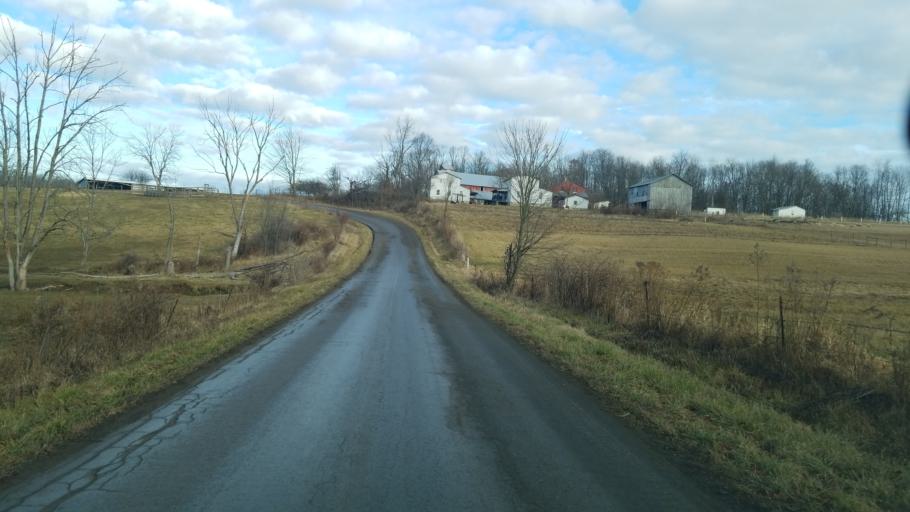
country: US
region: Ohio
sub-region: Knox County
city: Oak Hill
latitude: 40.3129
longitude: -82.2834
